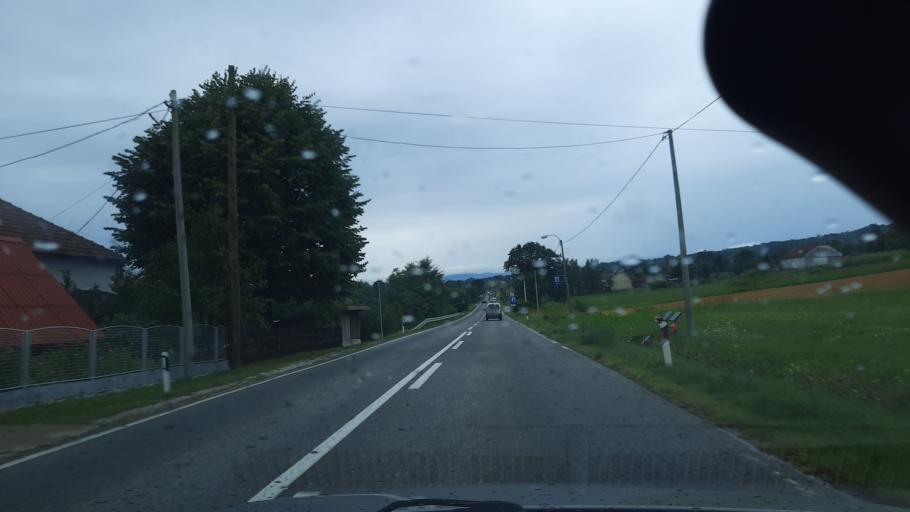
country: RS
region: Central Serbia
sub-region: Raski Okrug
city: Kraljevo
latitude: 43.7886
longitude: 20.7907
